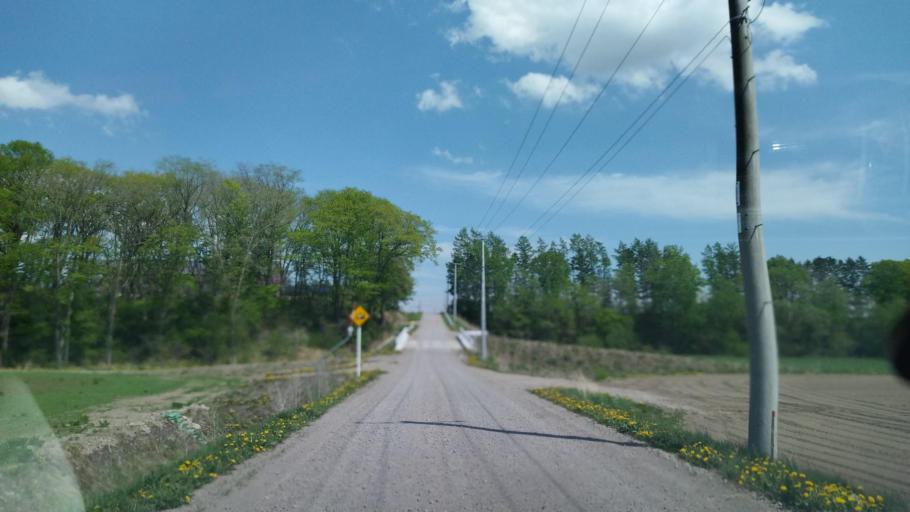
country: JP
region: Hokkaido
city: Otofuke
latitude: 43.1317
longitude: 143.2211
